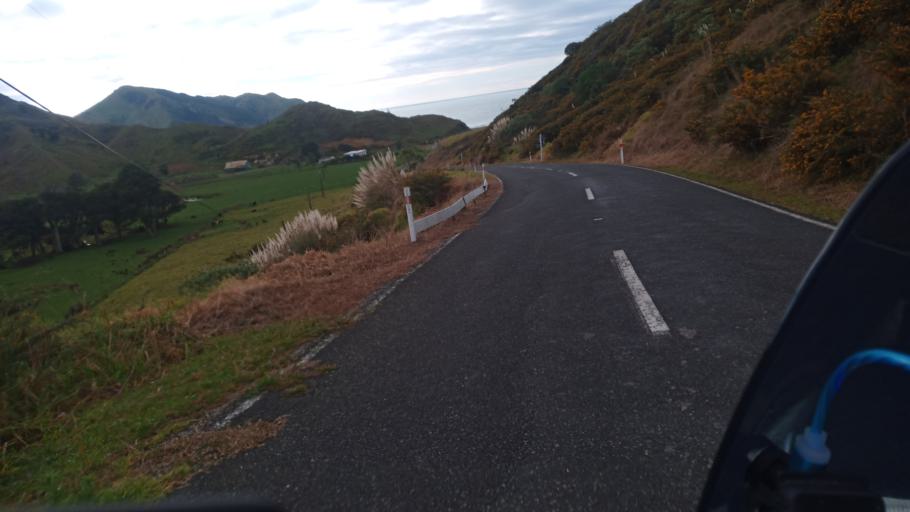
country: NZ
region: Gisborne
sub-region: Gisborne District
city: Gisborne
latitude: -38.3167
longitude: 178.3167
